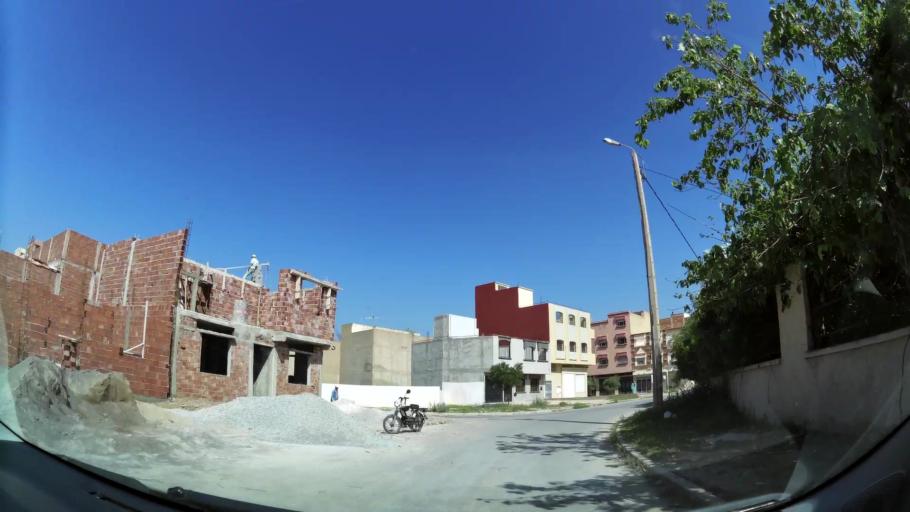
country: MA
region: Oriental
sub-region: Oujda-Angad
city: Oujda
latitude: 34.6949
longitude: -1.8770
